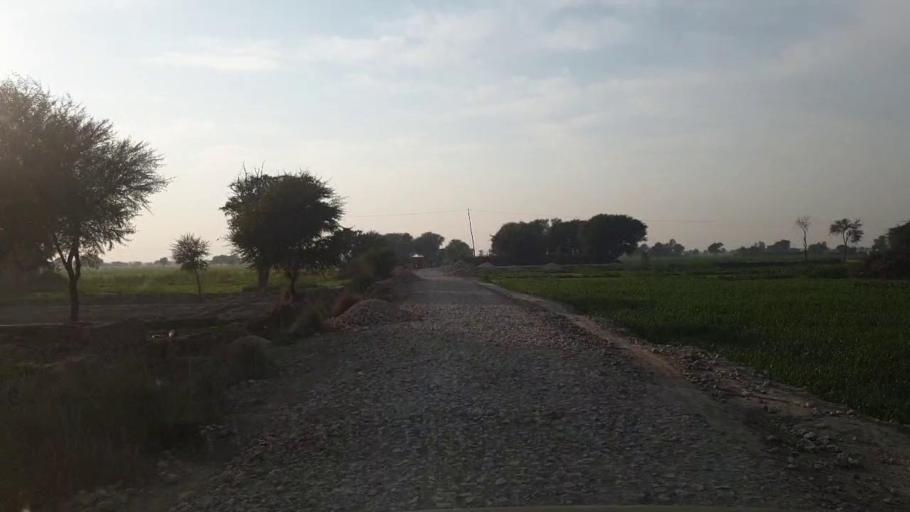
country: PK
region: Sindh
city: Shahpur Chakar
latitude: 26.1524
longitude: 68.6185
